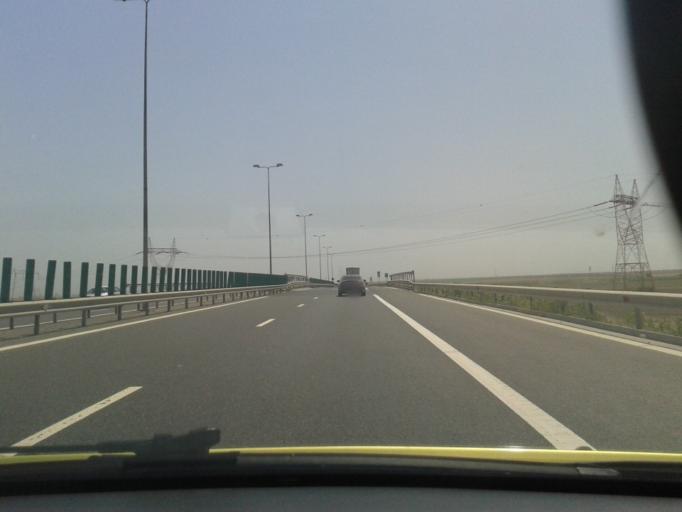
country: RO
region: Constanta
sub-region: Comuna Ovidiu
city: Ovidiu
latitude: 44.2284
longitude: 28.5502
